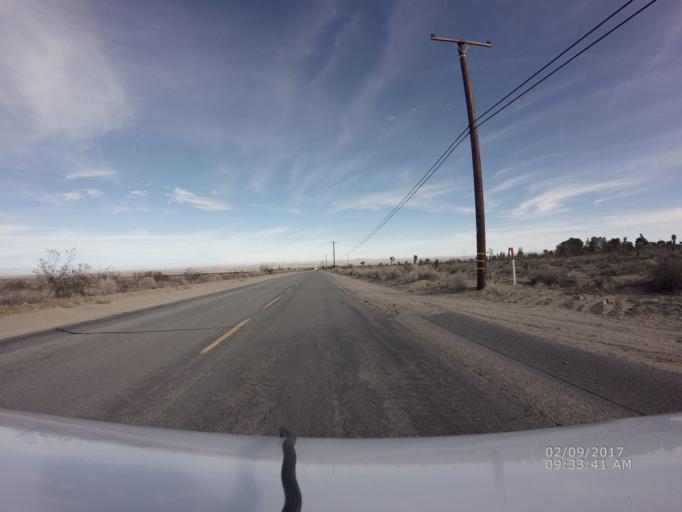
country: US
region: California
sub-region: Los Angeles County
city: Lake Los Angeles
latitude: 34.4808
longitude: -117.8354
